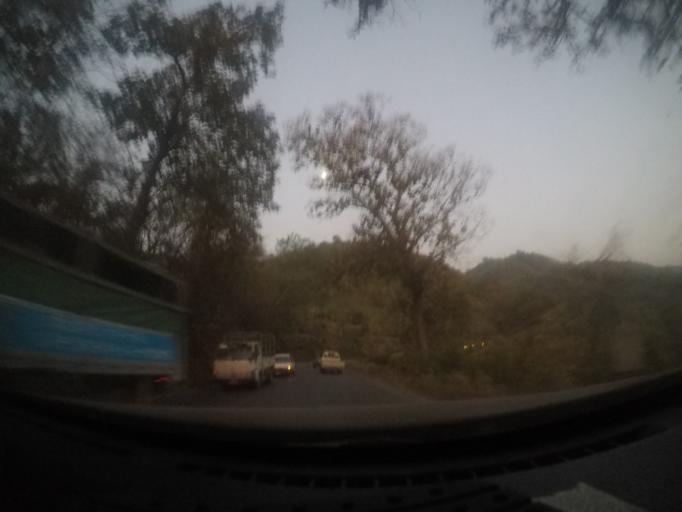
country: MM
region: Mandalay
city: Yamethin
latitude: 20.6932
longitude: 96.5058
